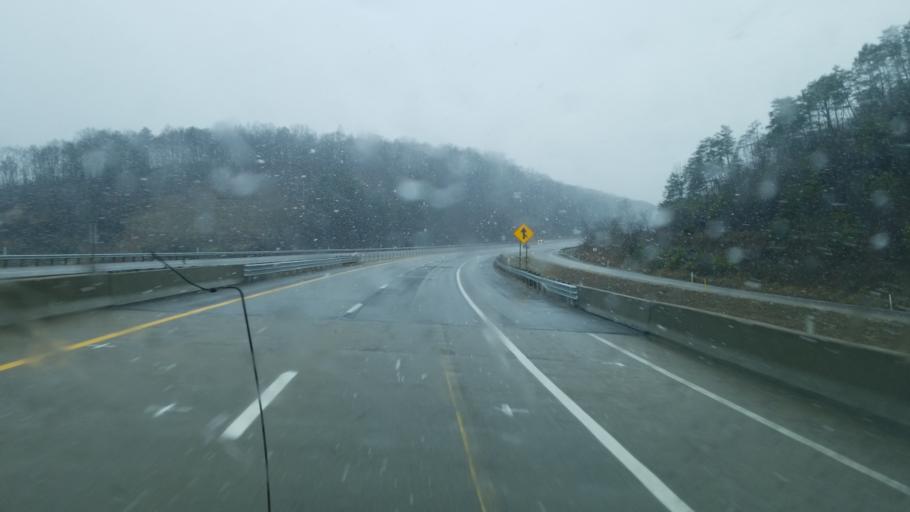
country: US
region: West Virginia
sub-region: Jackson County
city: Ravenswood
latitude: 39.0045
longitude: -81.6287
